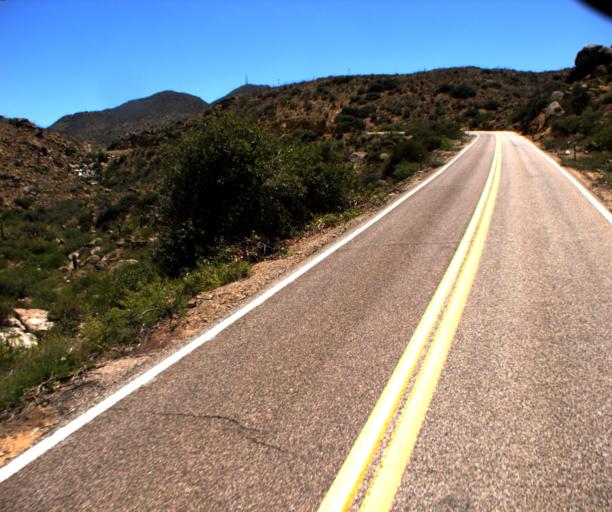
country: US
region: Arizona
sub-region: Yavapai County
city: Bagdad
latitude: 34.4526
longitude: -112.9765
